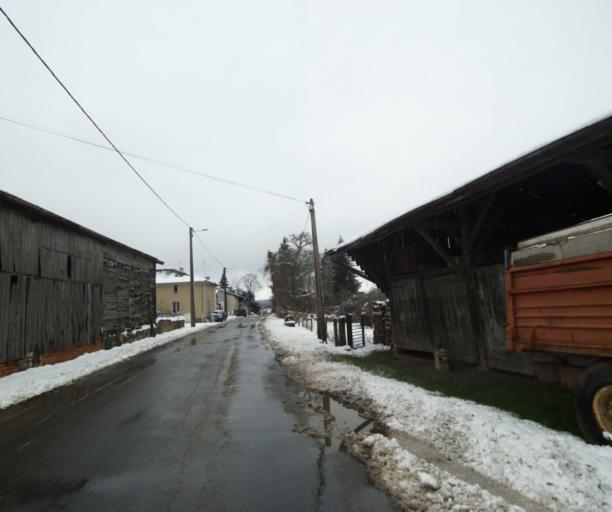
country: FR
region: Champagne-Ardenne
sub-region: Departement de la Haute-Marne
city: Laneuville-a-Remy
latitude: 48.4640
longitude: 4.9120
